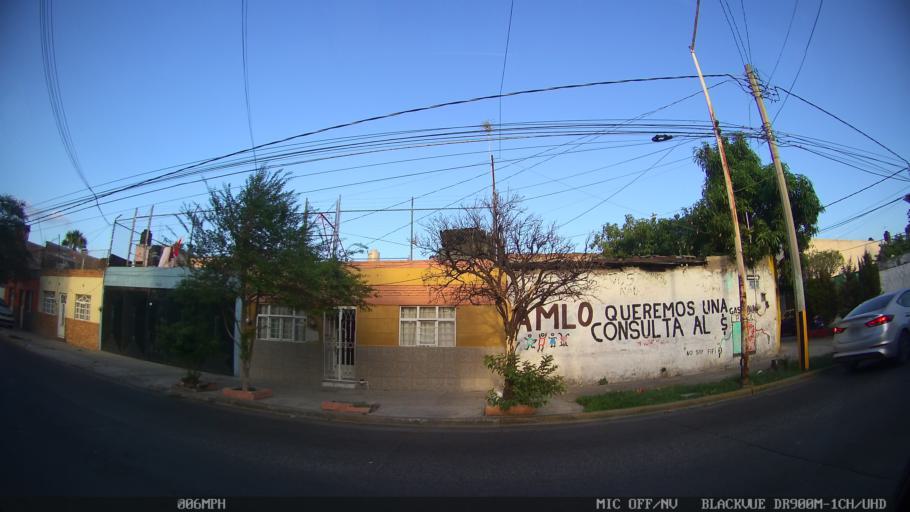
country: MX
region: Jalisco
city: Tlaquepaque
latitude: 20.6896
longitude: -103.3079
